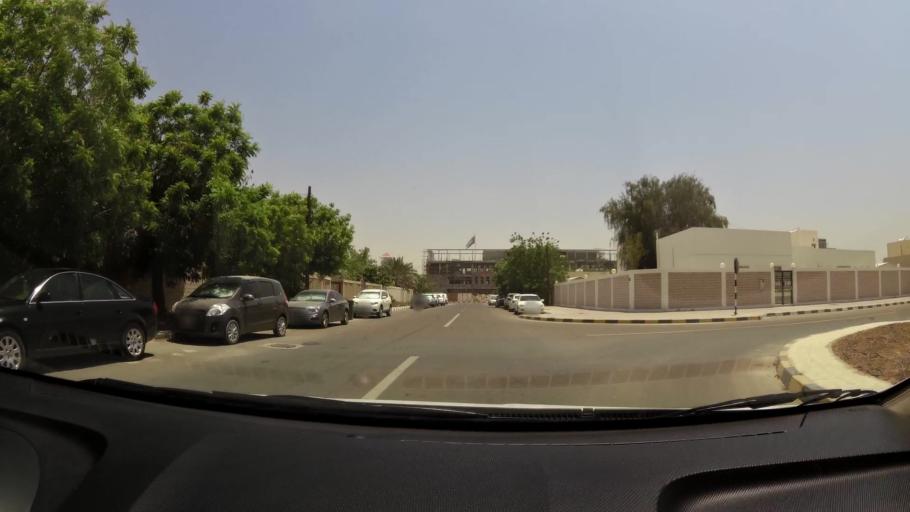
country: AE
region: Ajman
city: Ajman
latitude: 25.4195
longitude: 55.5022
